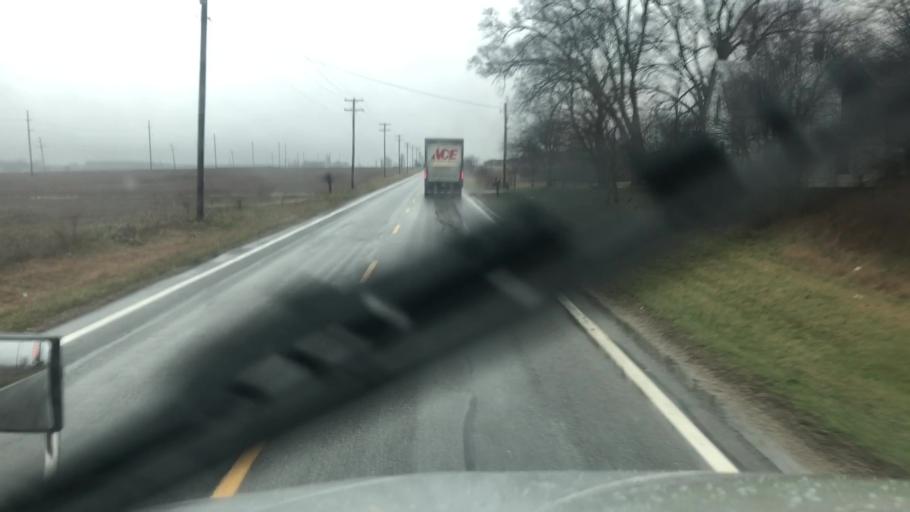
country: US
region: Ohio
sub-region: Union County
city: New California
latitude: 40.2106
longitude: -83.1833
